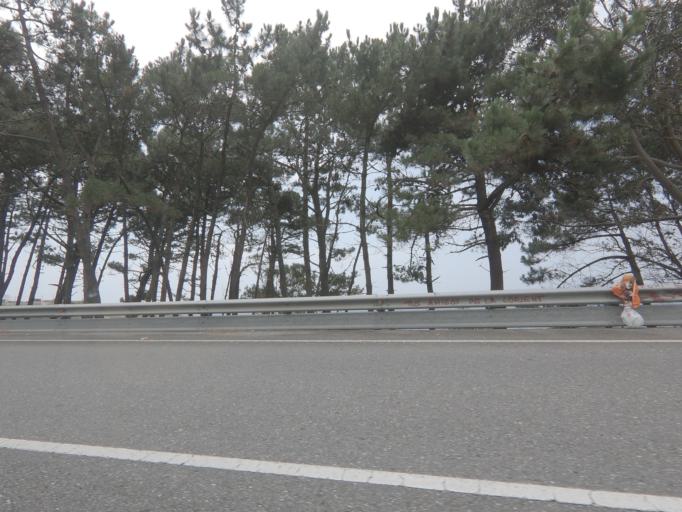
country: ES
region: Galicia
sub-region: Provincia de Pontevedra
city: Oia
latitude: 41.9544
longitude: -8.8833
